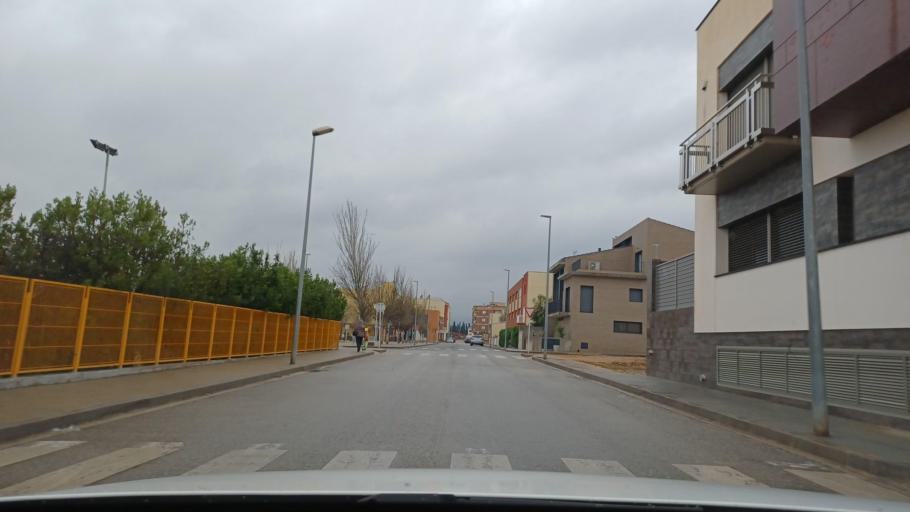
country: ES
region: Catalonia
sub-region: Provincia de Tarragona
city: Amposta
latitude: 40.7054
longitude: 0.5742
